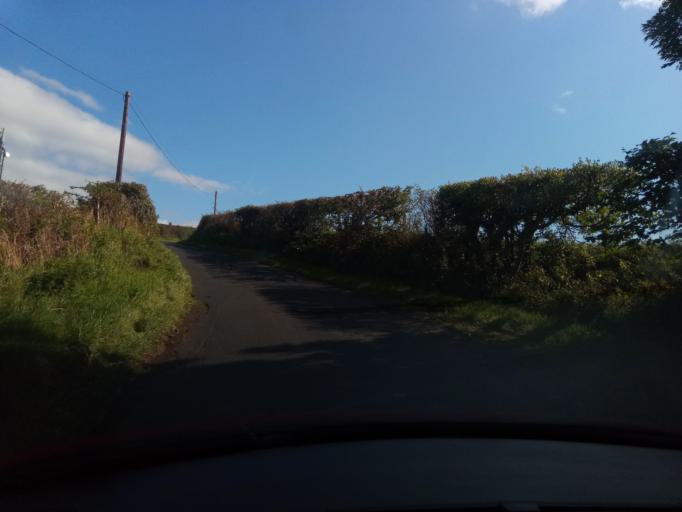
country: GB
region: Scotland
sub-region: The Scottish Borders
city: Jedburgh
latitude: 55.5134
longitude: -2.4881
